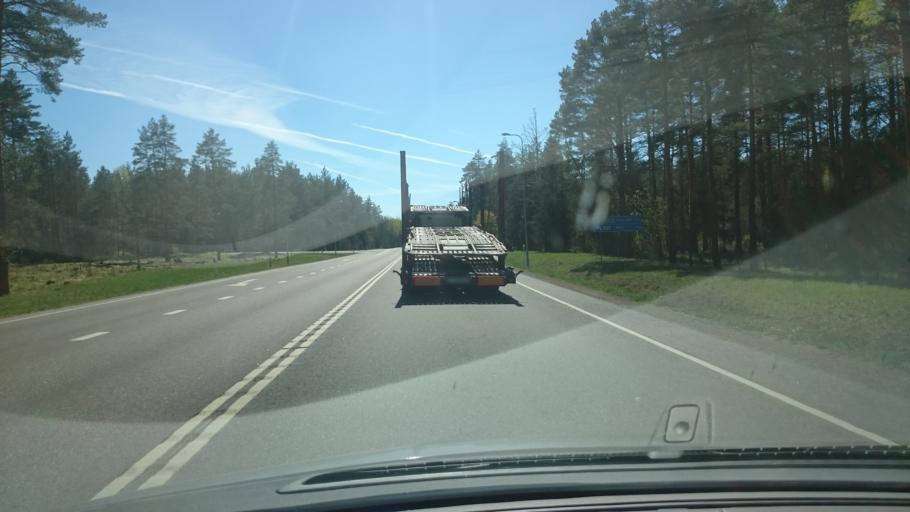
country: EE
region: Ida-Virumaa
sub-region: Toila vald
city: Voka
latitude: 59.3848
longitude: 27.5696
